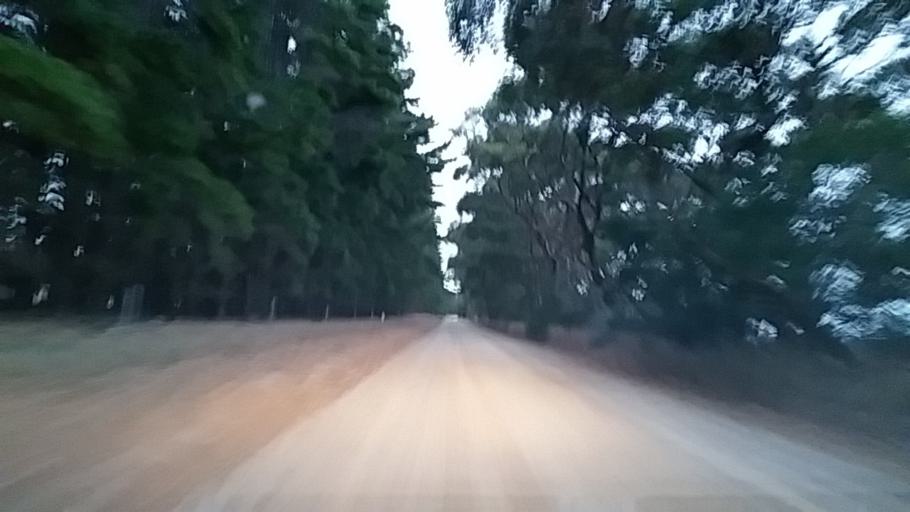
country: AU
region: South Australia
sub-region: Yankalilla
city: Normanville
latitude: -35.6100
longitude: 138.1830
